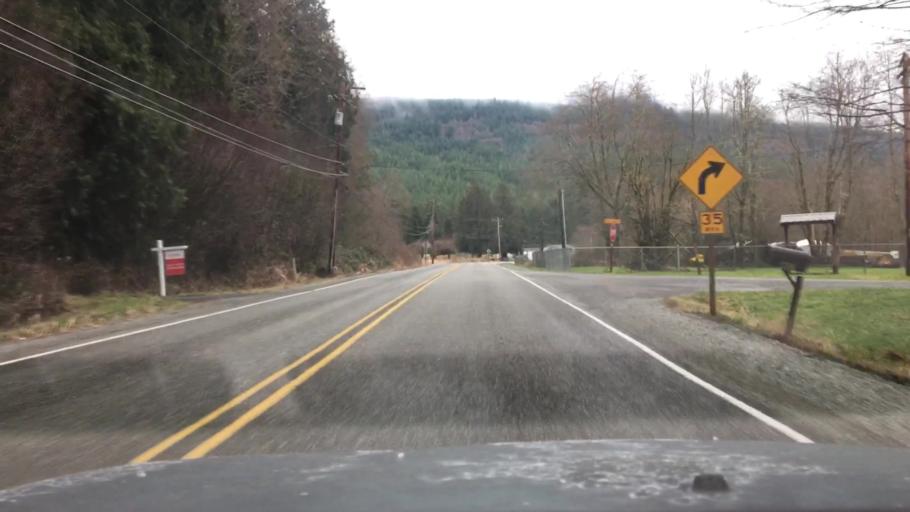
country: US
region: Washington
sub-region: Whatcom County
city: Sudden Valley
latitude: 48.6396
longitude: -122.3140
